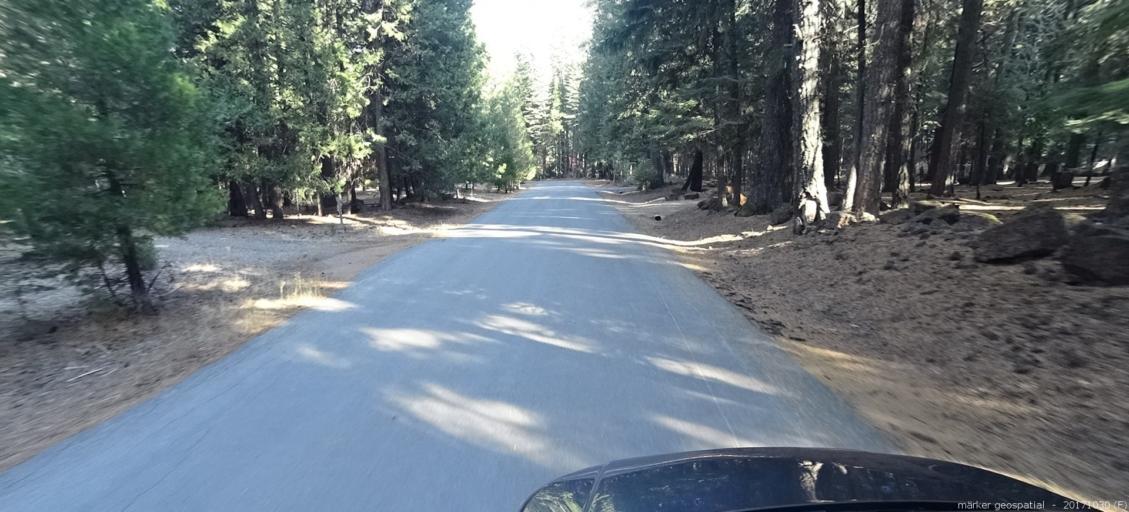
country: US
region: California
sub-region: Shasta County
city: Shingletown
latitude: 40.5515
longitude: -121.7318
